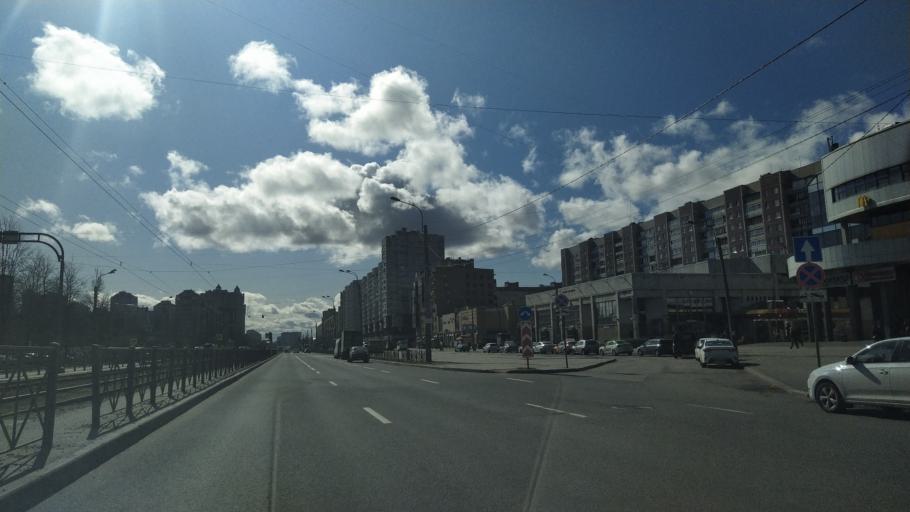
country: RU
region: Leningrad
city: Parnas
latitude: 60.0521
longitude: 30.3341
